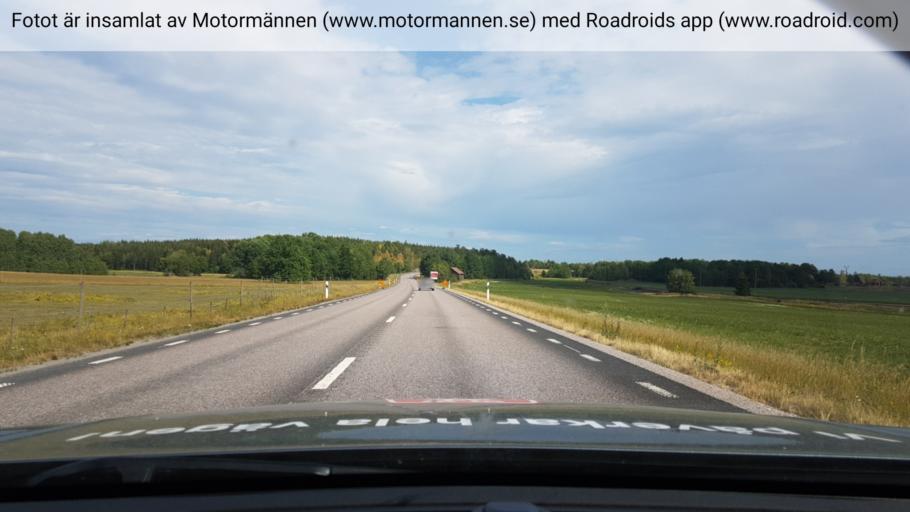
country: SE
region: Uppsala
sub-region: Enkopings Kommun
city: Orsundsbro
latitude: 59.8628
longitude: 17.3560
